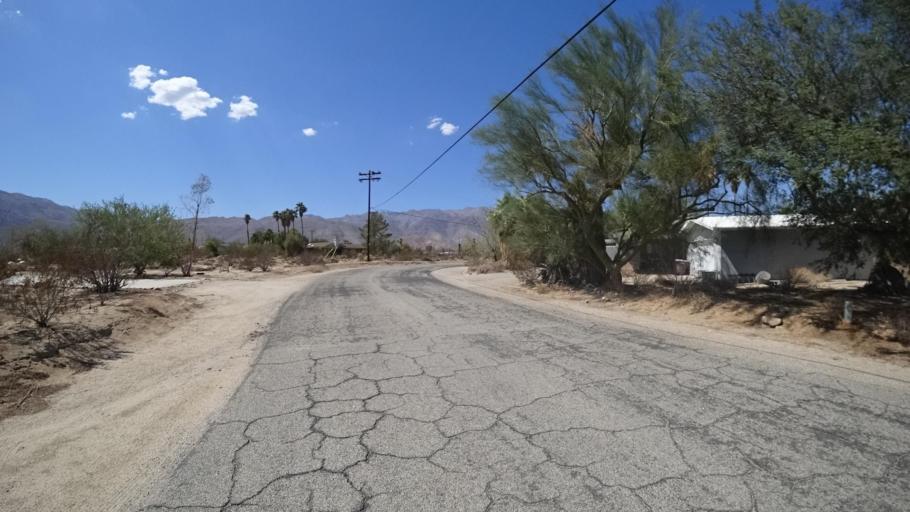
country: US
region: California
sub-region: San Diego County
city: Borrego Springs
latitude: 33.2229
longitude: -116.3655
